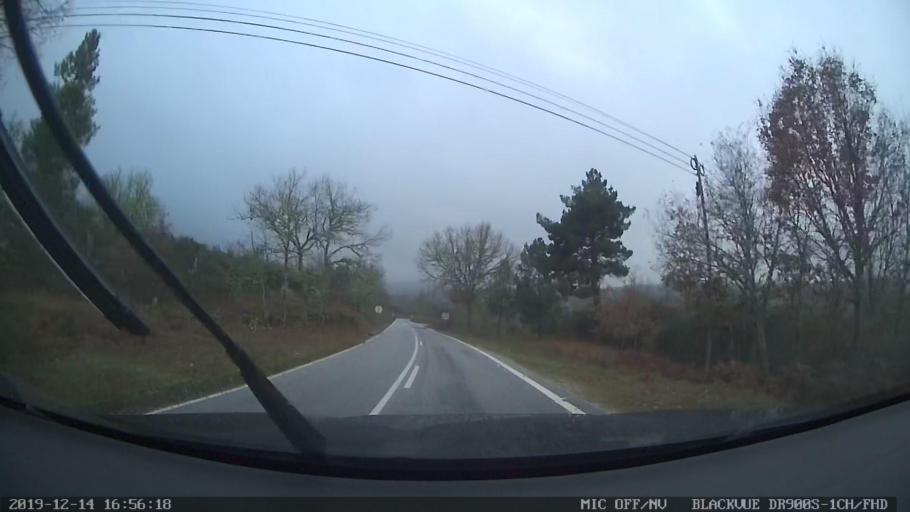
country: PT
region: Vila Real
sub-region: Murca
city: Murca
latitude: 41.4347
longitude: -7.5386
